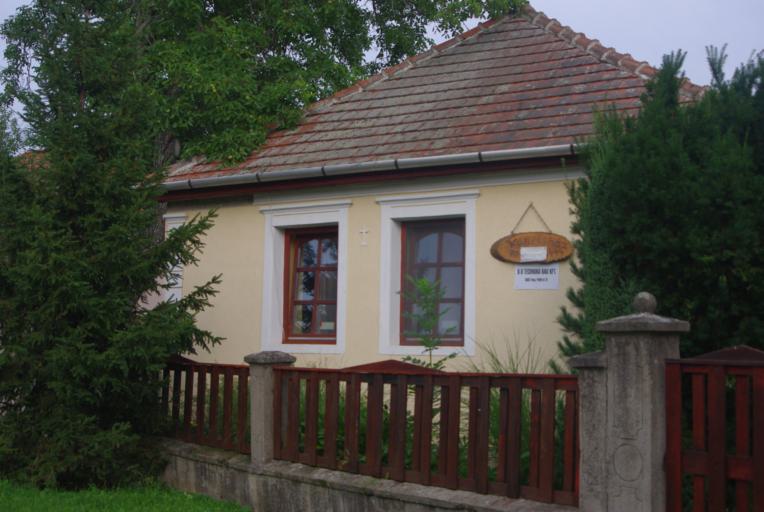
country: HU
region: Borsod-Abauj-Zemplen
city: Gonc
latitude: 48.3904
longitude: 21.2860
